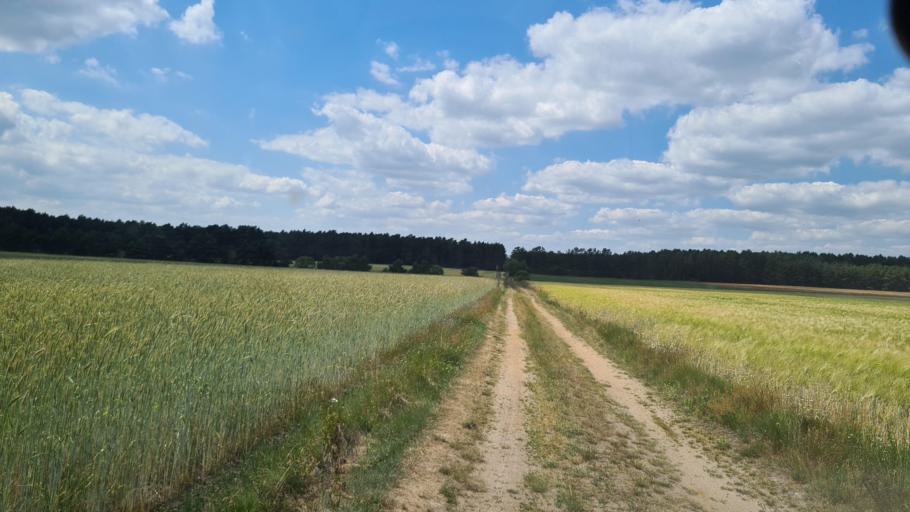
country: DE
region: Brandenburg
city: Sallgast
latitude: 51.6529
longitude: 13.8169
